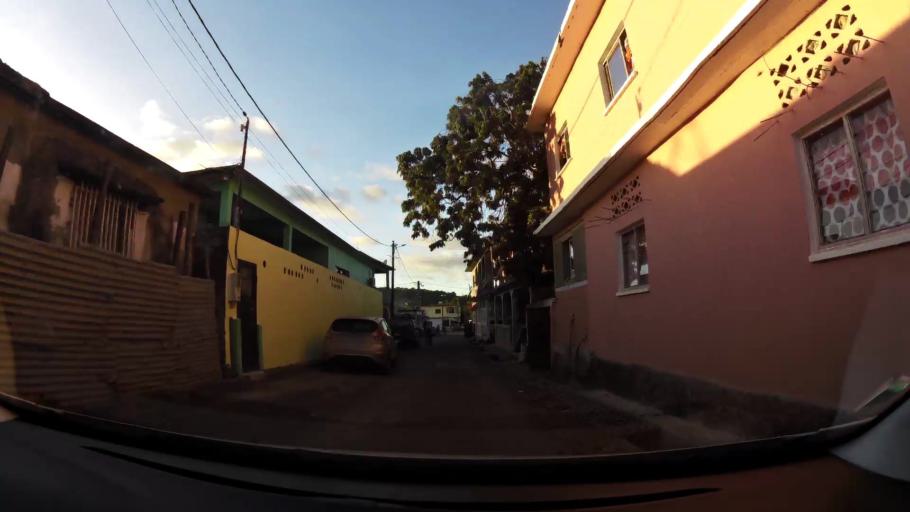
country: YT
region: Dembeni
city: Dembeni
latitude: -12.8448
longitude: 45.1907
